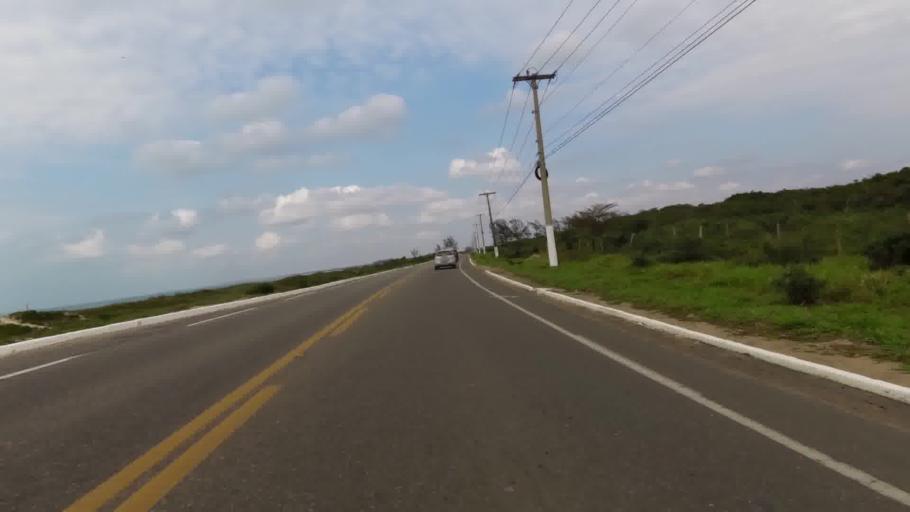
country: BR
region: Espirito Santo
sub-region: Piuma
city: Piuma
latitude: -20.9151
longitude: -40.7871
